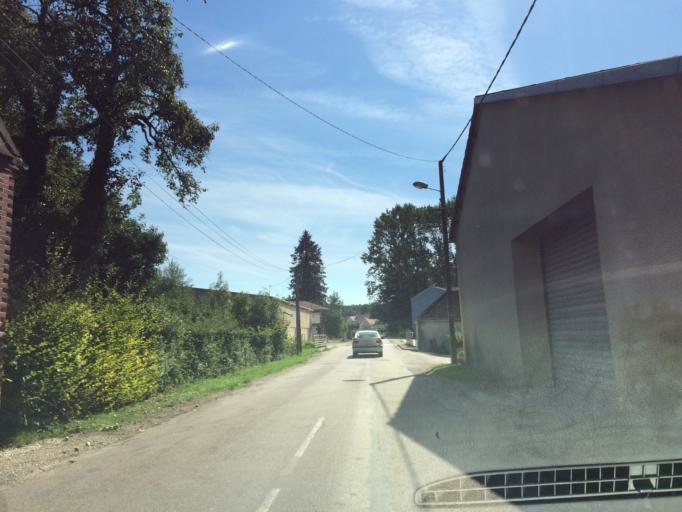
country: FR
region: Bourgogne
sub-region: Departement de l'Yonne
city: Aillant-sur-Tholon
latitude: 47.8341
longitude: 3.3638
